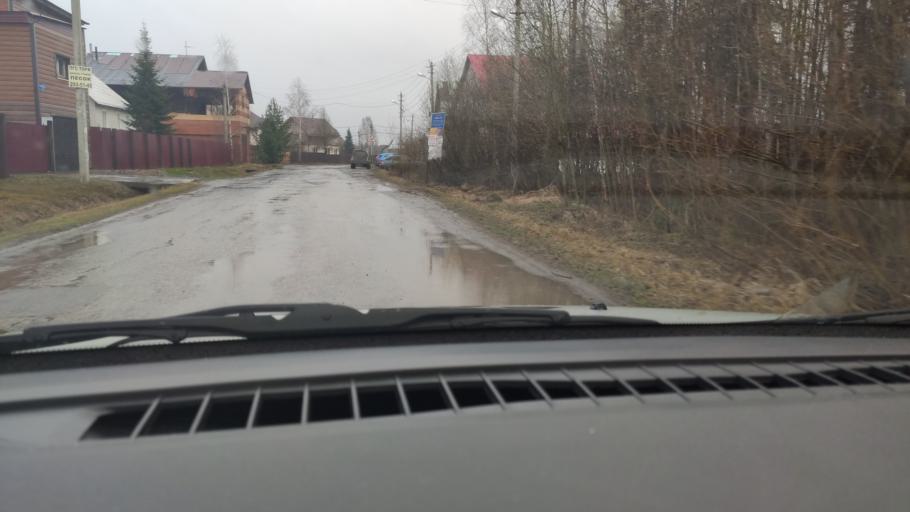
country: RU
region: Perm
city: Ferma
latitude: 57.9441
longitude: 56.4161
